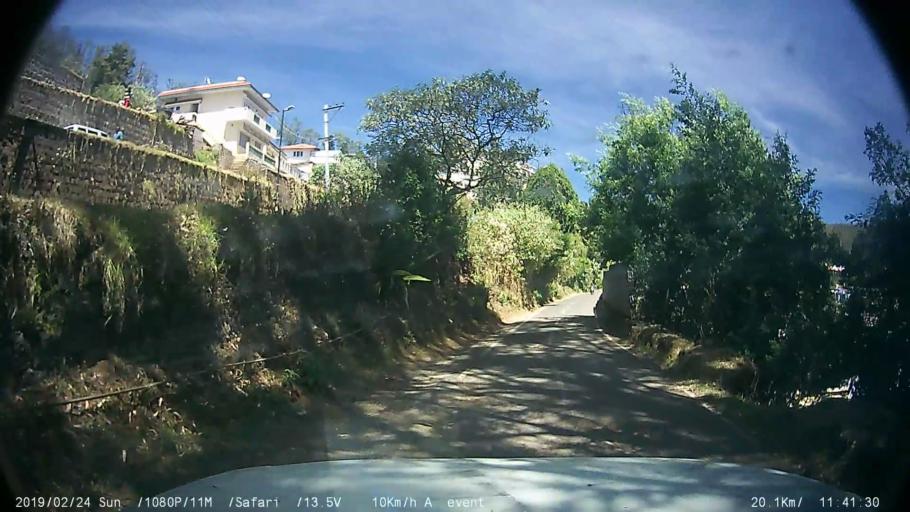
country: IN
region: Tamil Nadu
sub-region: Nilgiri
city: Ooty
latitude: 11.4176
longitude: 76.7049
